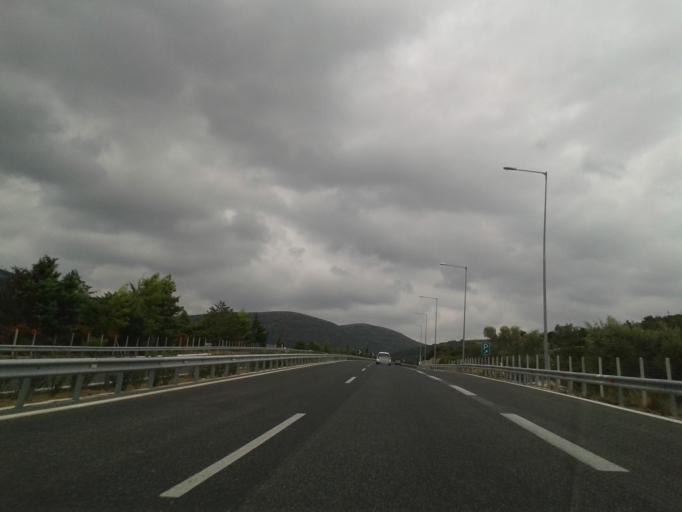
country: GR
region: Peloponnese
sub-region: Nomos Korinthias
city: Ayios Vasilios
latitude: 37.8053
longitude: 22.7599
